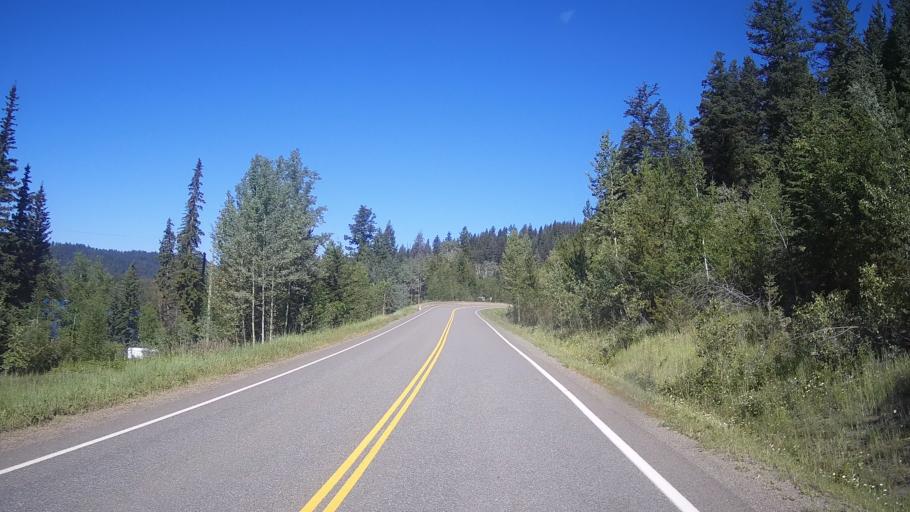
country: CA
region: British Columbia
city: Kamloops
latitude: 51.4708
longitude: -120.5357
